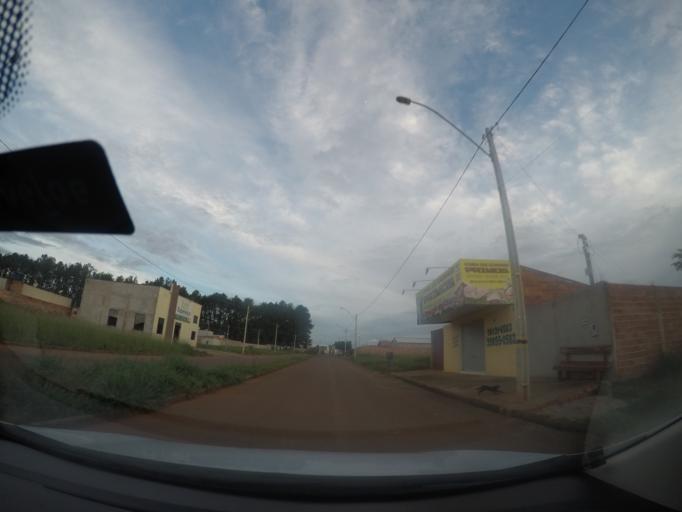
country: BR
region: Goias
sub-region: Goianira
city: Goianira
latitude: -16.5672
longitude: -49.3749
